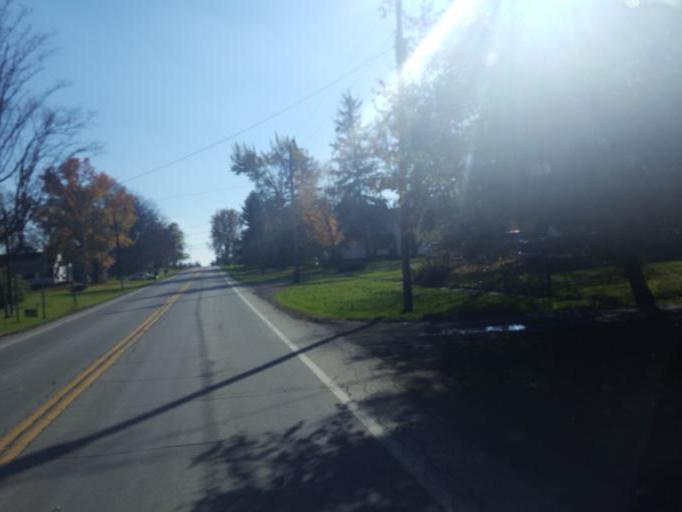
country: US
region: Ohio
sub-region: Wayne County
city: West Salem
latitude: 41.0277
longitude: -82.2220
